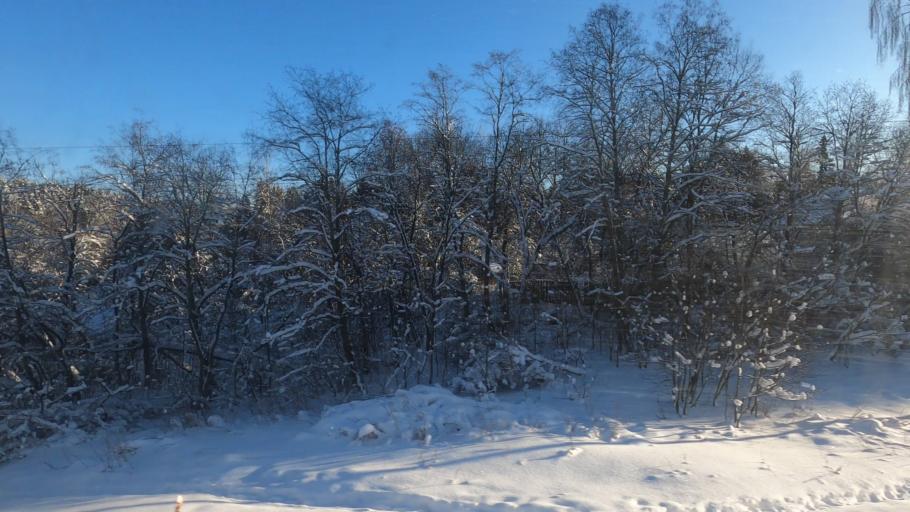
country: RU
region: Moskovskaya
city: Novo-Nikol'skoye
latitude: 56.5492
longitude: 37.5615
